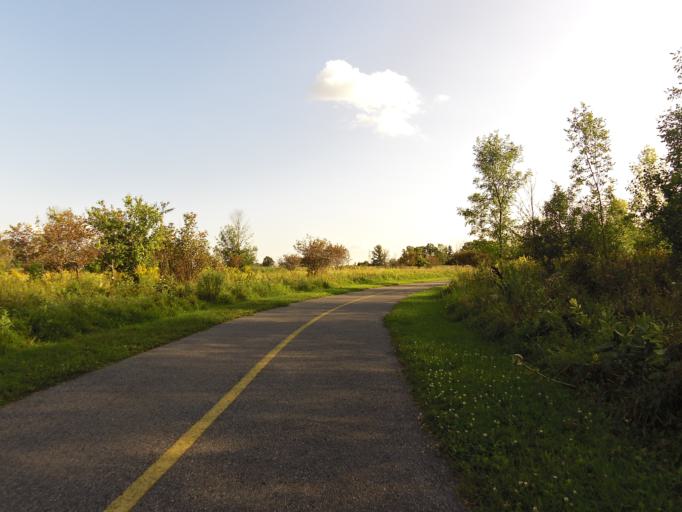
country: CA
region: Ontario
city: Bells Corners
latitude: 45.3375
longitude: -75.8856
